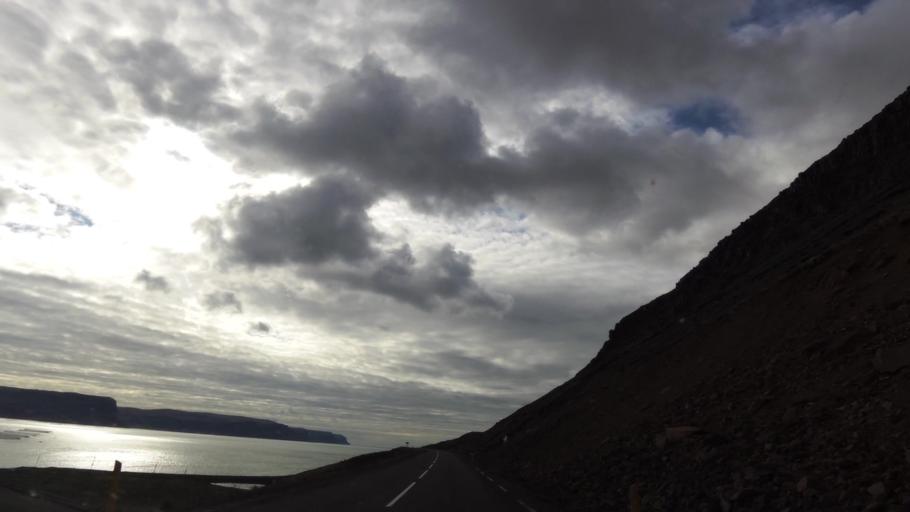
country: IS
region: West
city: Olafsvik
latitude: 65.5802
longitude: -23.9528
